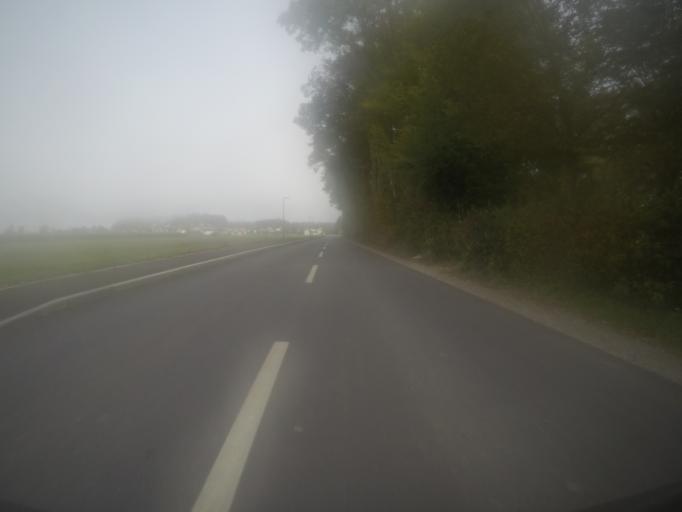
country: SI
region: Domzale
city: Dob
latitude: 46.1619
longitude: 14.6274
